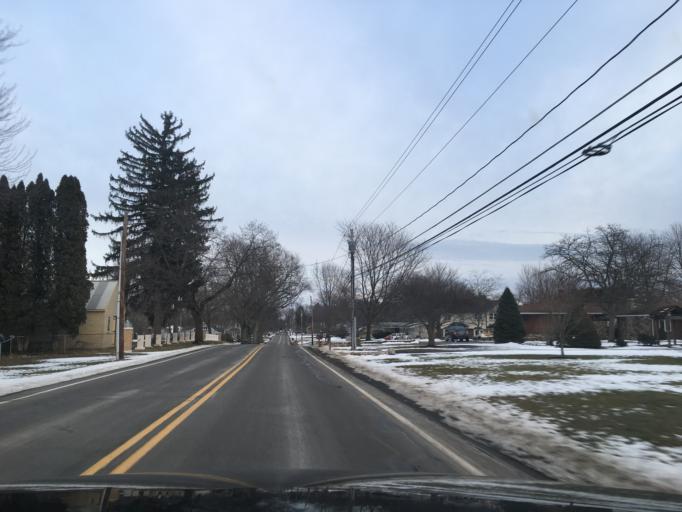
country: US
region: New York
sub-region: Ontario County
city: Manchester
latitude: 42.9546
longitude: -77.2381
